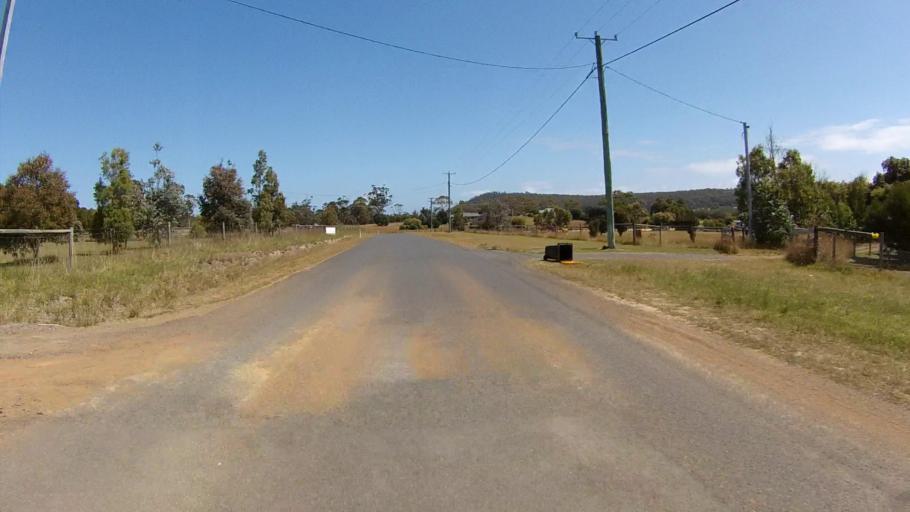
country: AU
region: Tasmania
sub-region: Clarence
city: Sandford
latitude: -42.9556
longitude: 147.4837
